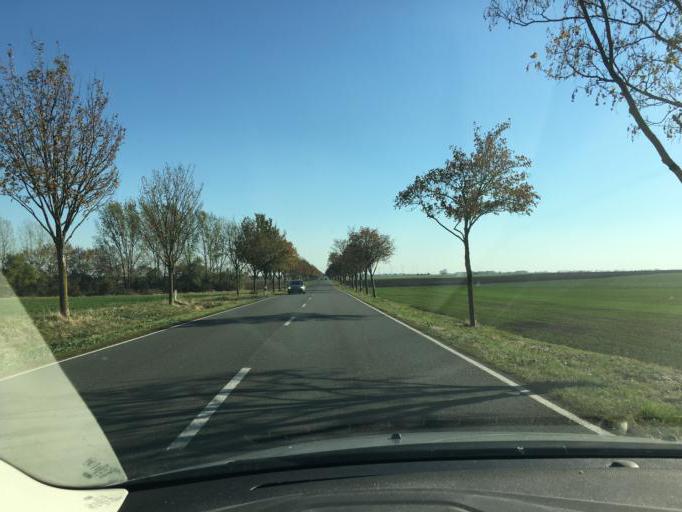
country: DE
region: Saxony-Anhalt
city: Wanzleben
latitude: 52.0278
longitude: 11.4857
